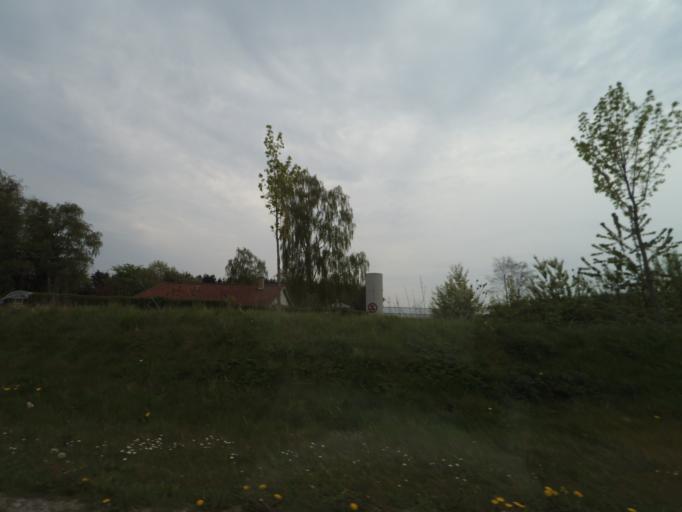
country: DK
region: South Denmark
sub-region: Faaborg-Midtfyn Kommune
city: Arslev
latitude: 55.3043
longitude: 10.4460
